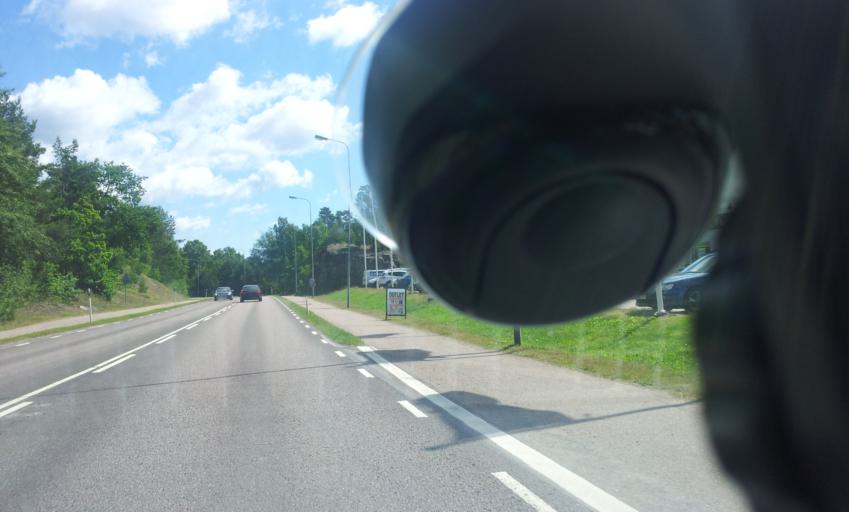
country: SE
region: Kalmar
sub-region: Oskarshamns Kommun
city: Oskarshamn
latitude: 57.2524
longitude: 16.4524
